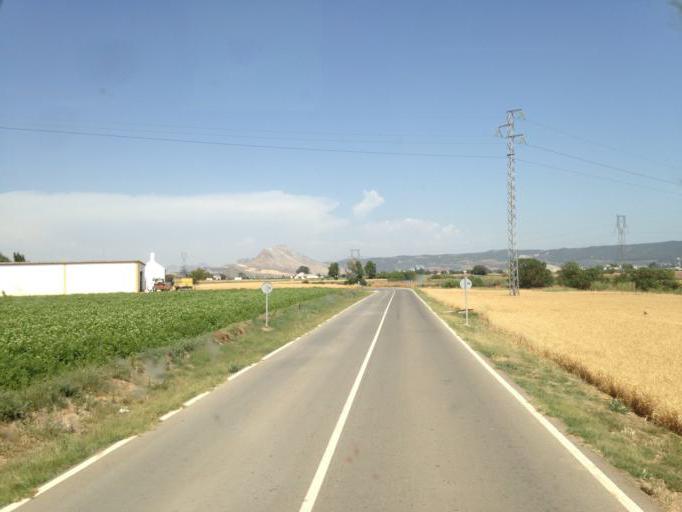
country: ES
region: Andalusia
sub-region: Provincia de Malaga
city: Antequera
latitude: 37.0574
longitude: -4.5779
